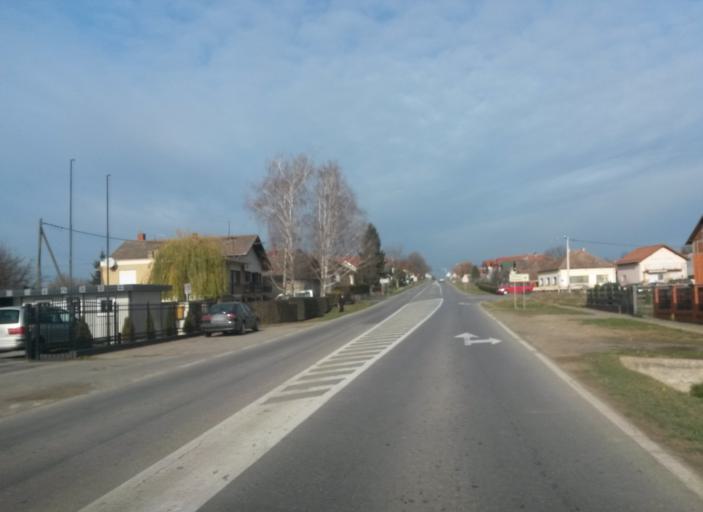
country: HR
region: Osjecko-Baranjska
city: Viskovci
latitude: 45.3450
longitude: 18.4215
